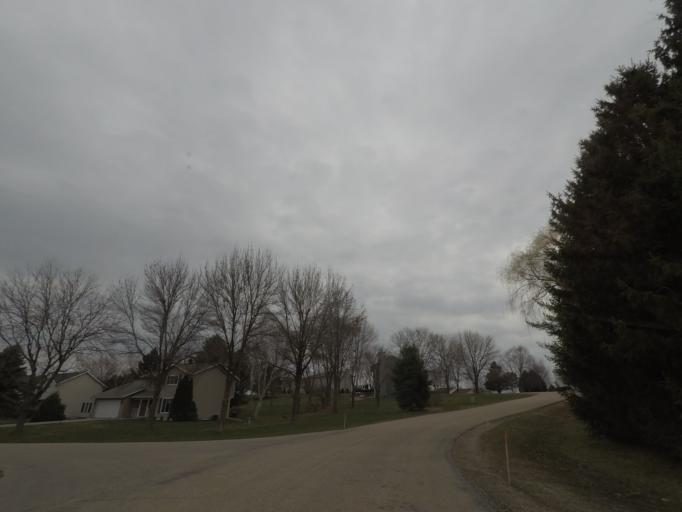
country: US
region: Wisconsin
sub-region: Dane County
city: Middleton
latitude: 43.1092
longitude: -89.5526
